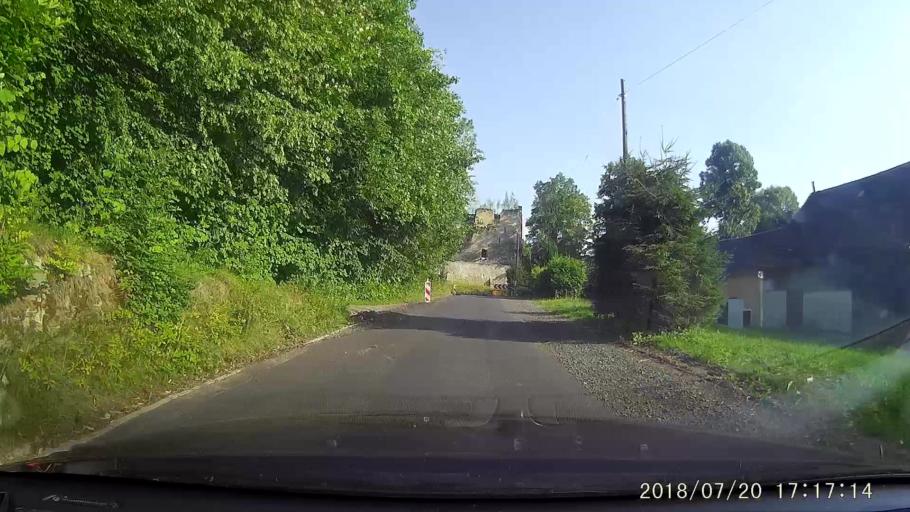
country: PL
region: Lower Silesian Voivodeship
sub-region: Powiat lubanski
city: Lesna
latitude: 50.9985
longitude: 15.2841
